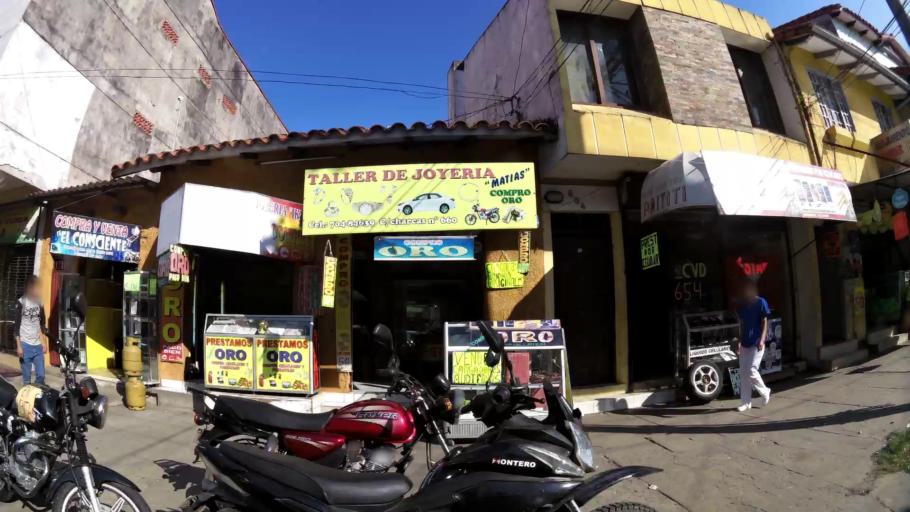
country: BO
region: Santa Cruz
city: Santa Cruz de la Sierra
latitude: -17.7798
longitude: -63.1743
